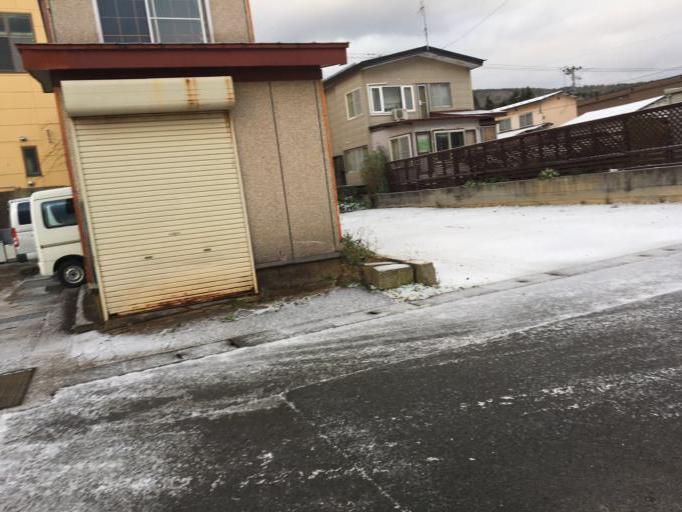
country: JP
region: Aomori
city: Mutsu
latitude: 41.2763
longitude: 141.1571
